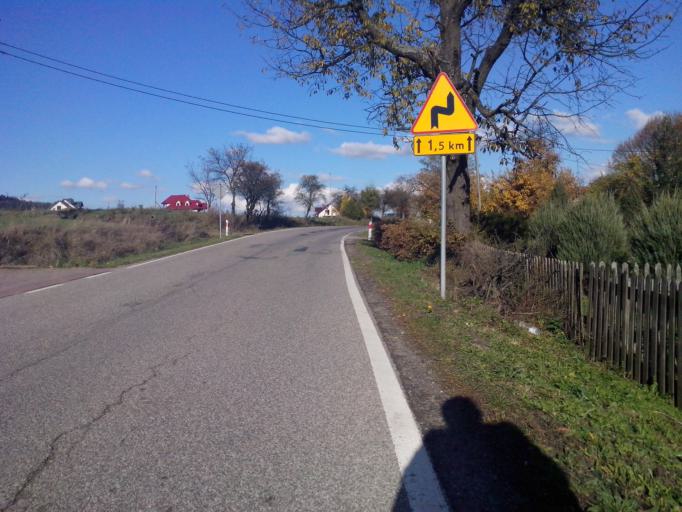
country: PL
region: Subcarpathian Voivodeship
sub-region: Powiat krosnienski
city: Korczyna
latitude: 49.7723
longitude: 21.8501
